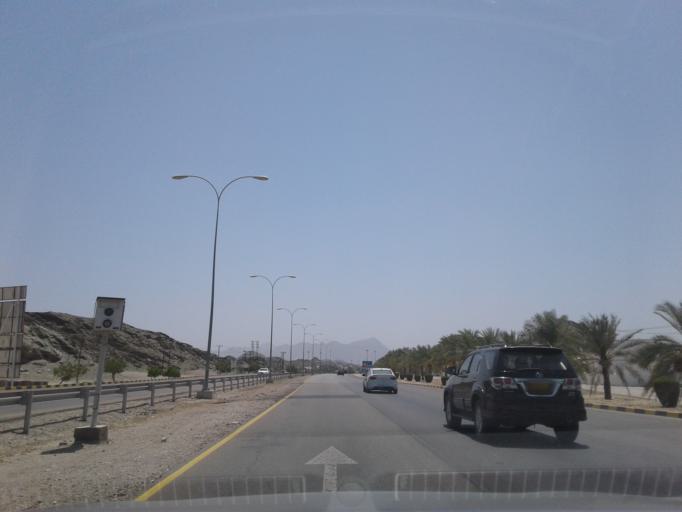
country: OM
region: Muhafazat Masqat
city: Bawshar
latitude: 23.4718
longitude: 58.4948
